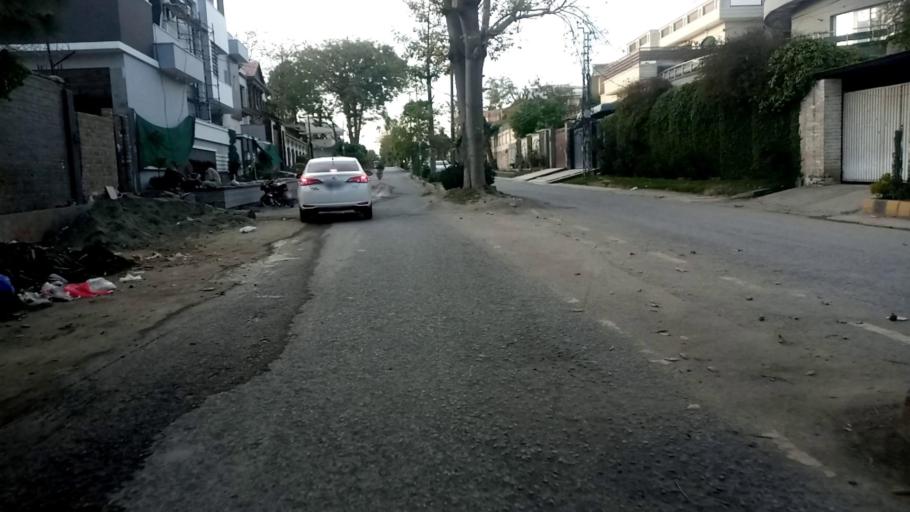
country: PK
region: Khyber Pakhtunkhwa
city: Peshawar
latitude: 34.0200
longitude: 71.5531
